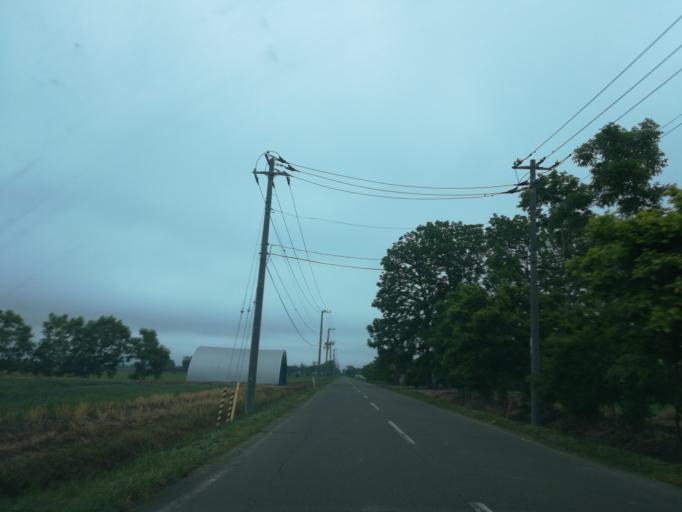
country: JP
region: Hokkaido
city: Ebetsu
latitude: 43.0674
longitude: 141.6367
